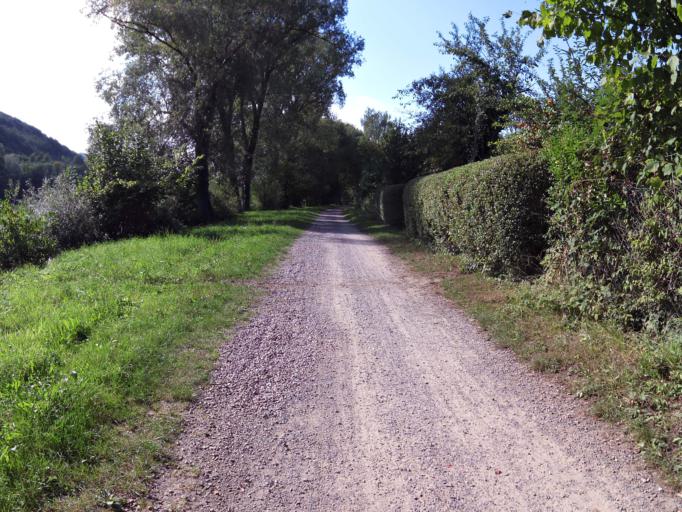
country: DE
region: Baden-Wuerttemberg
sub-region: Freiburg Region
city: Bad Sackingen
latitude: 47.5452
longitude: 7.9409
